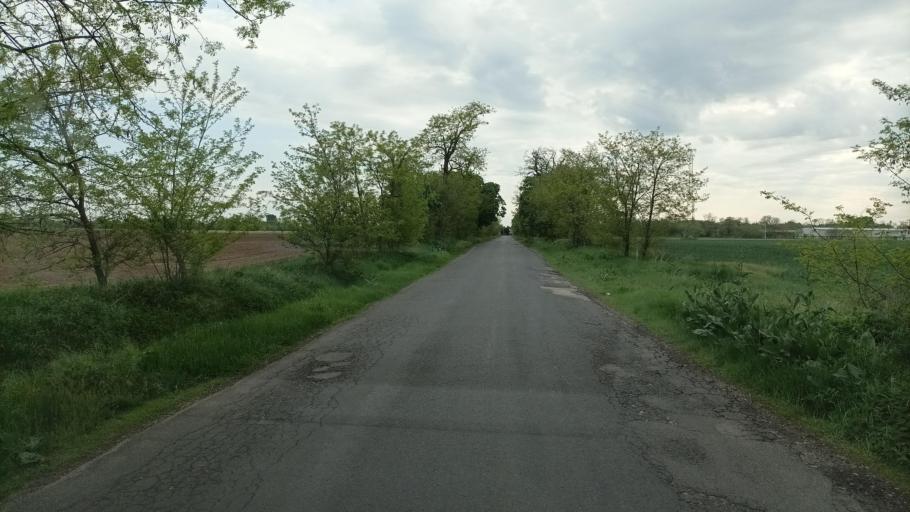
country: HU
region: Pest
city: Nyaregyhaza
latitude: 47.2701
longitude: 19.5186
